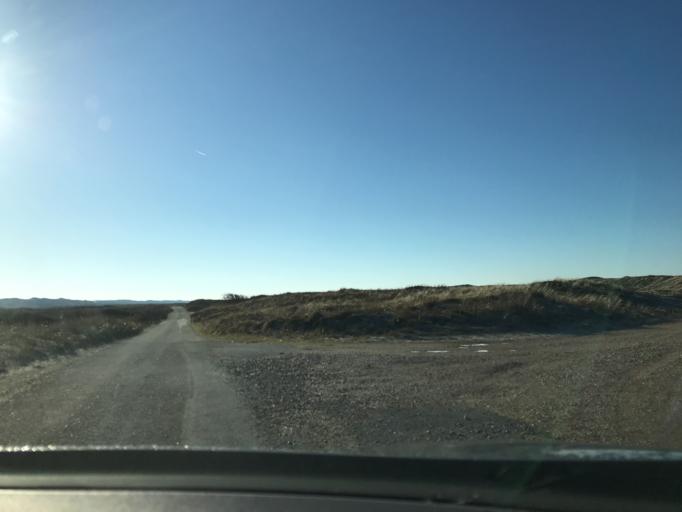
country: DK
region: South Denmark
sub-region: Varde Kommune
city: Oksbol
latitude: 55.8010
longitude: 8.1817
